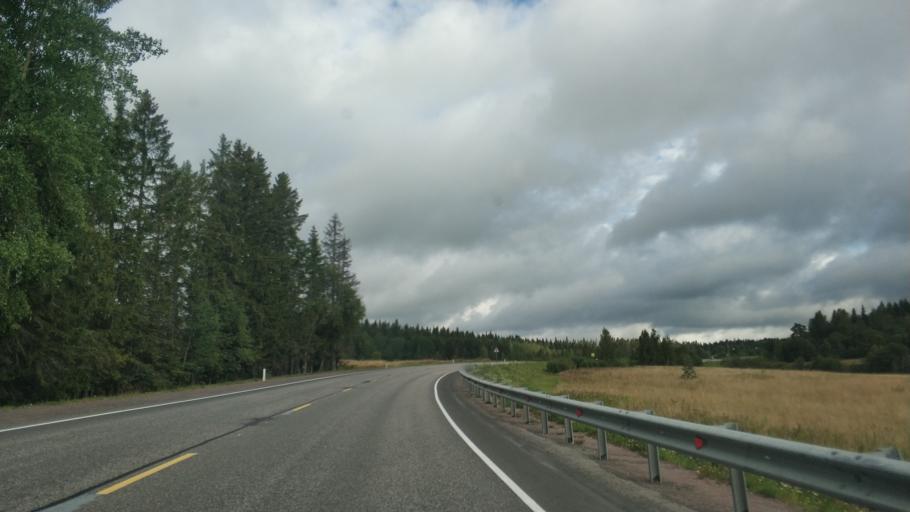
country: RU
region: Republic of Karelia
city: Khelyulya
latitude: 61.7978
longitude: 30.6164
